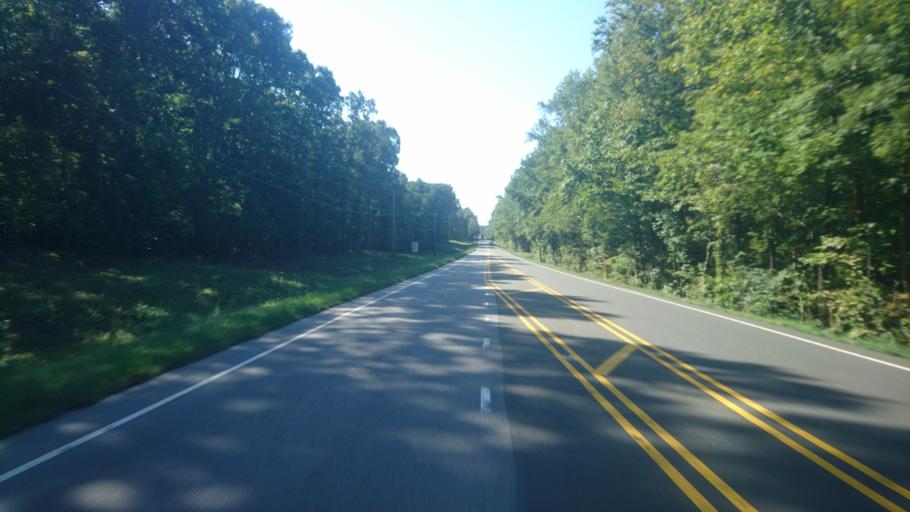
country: US
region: North Carolina
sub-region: Orange County
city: Hillsborough
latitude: 36.0365
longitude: -79.0819
